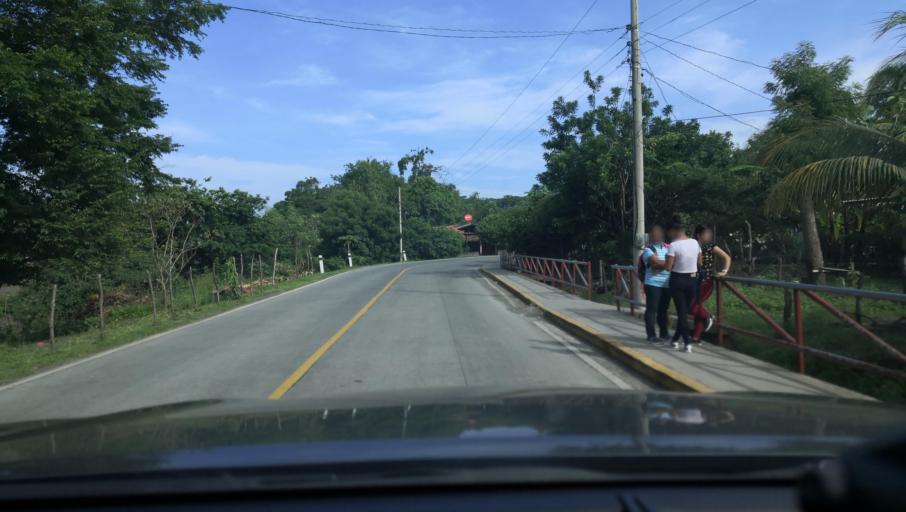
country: NI
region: Masaya
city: Tisma
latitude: 12.1497
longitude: -85.8401
